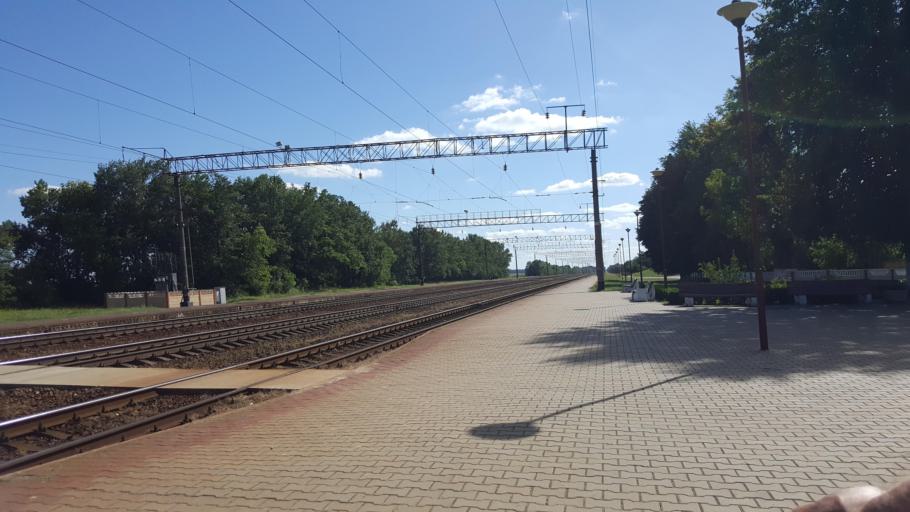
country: BY
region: Brest
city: Kobryn
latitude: 52.3402
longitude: 24.2362
